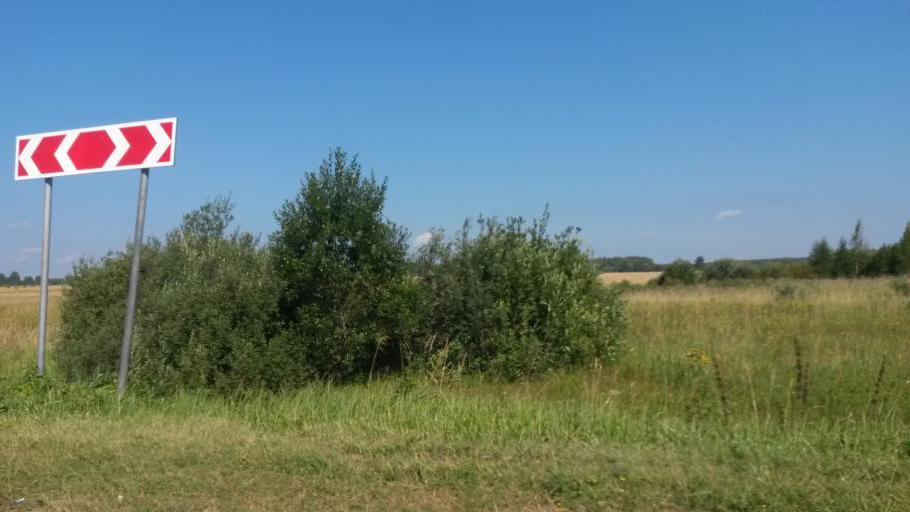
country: RU
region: Jaroslavl
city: Tutayev
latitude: 57.9494
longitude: 39.4587
